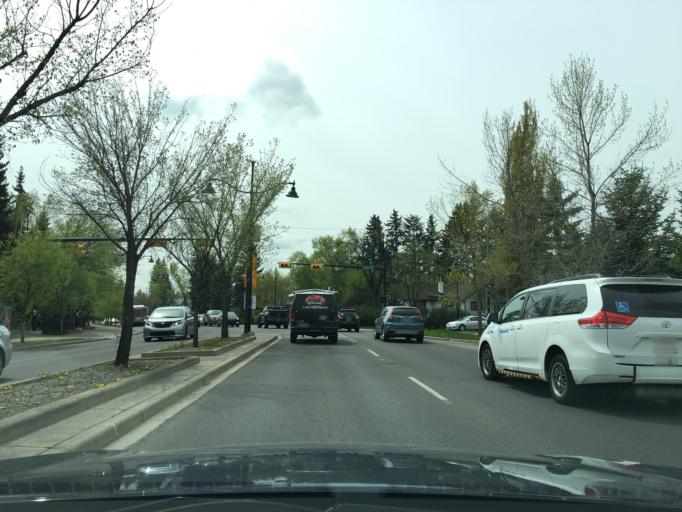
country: CA
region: Alberta
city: Calgary
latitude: 51.0268
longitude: -114.0787
